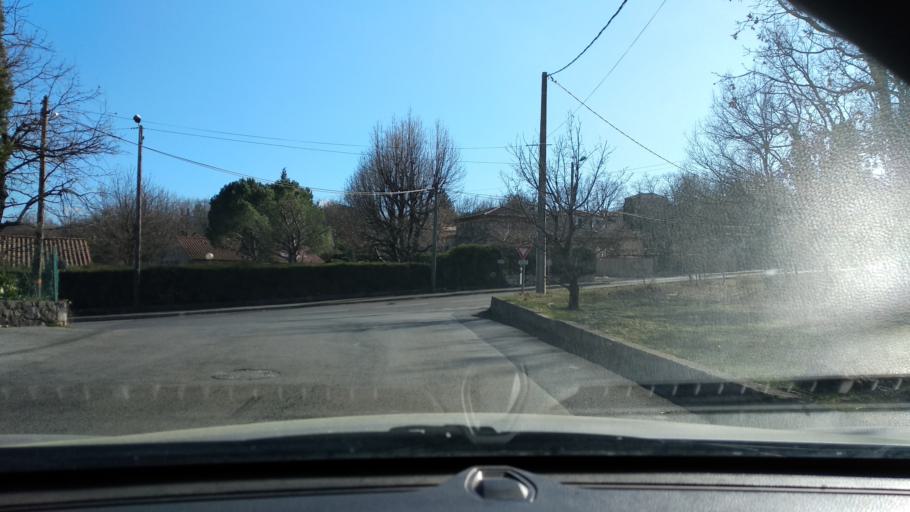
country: FR
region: Provence-Alpes-Cote d'Azur
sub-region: Departement des Alpes-Maritimes
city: Saint-Cezaire-sur-Siagne
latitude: 43.6506
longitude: 6.8005
